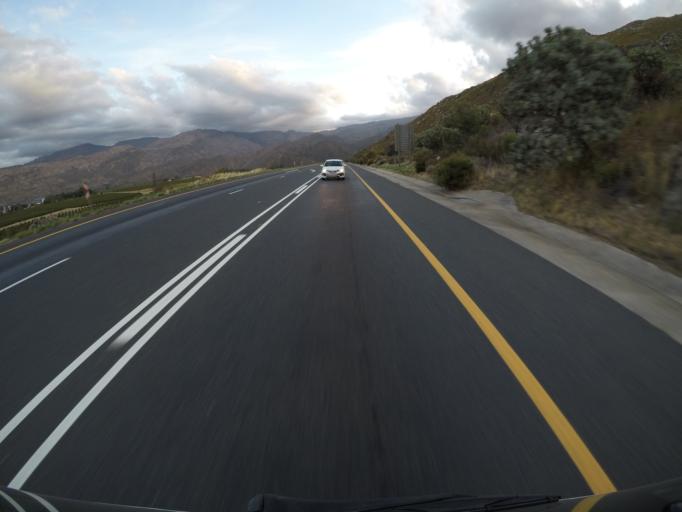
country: ZA
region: Western Cape
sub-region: Cape Winelands District Municipality
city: Worcester
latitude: -33.6959
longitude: 19.2649
